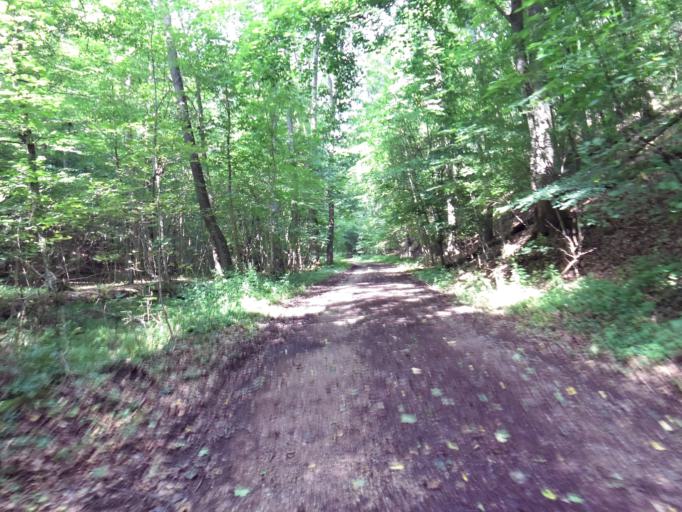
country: DE
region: Rheinland-Pfalz
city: Steinbach am Donnersberg
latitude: 49.5986
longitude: 7.9296
